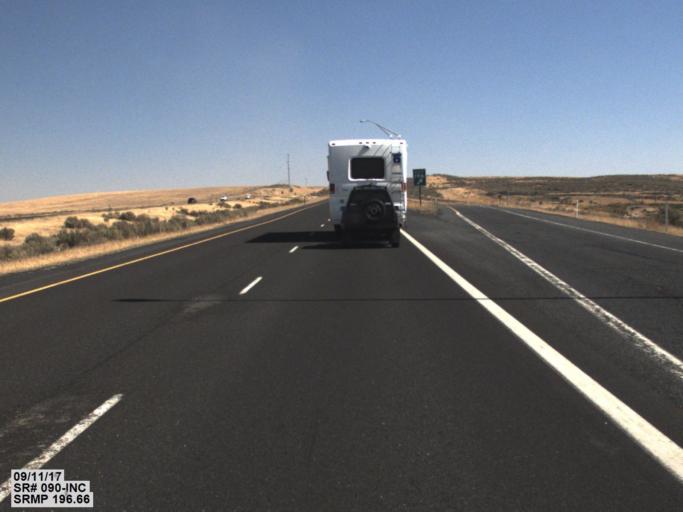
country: US
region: Washington
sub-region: Grant County
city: Warden
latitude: 47.0869
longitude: -118.8805
